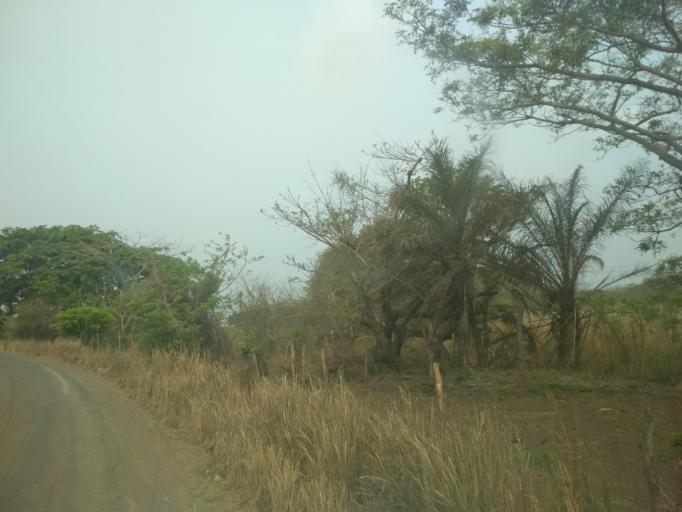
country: MX
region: Veracruz
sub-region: Veracruz
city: Delfino Victoria (Santa Fe)
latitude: 19.2105
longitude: -96.2587
